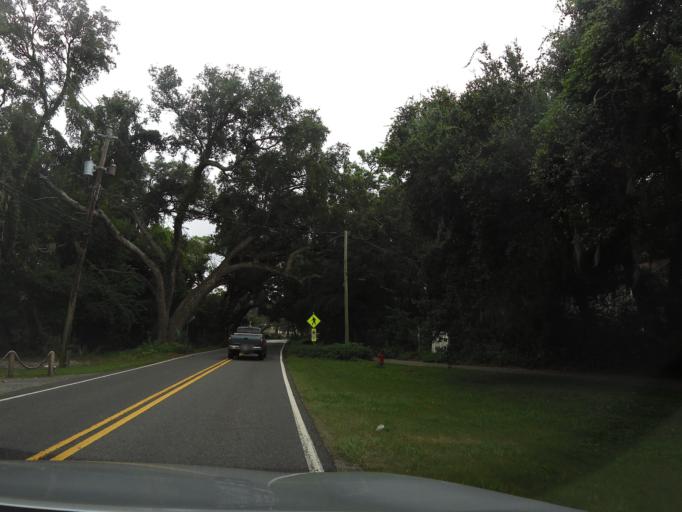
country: US
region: Georgia
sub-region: Glynn County
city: Saint Simons Island
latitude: 31.1499
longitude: -81.3809
